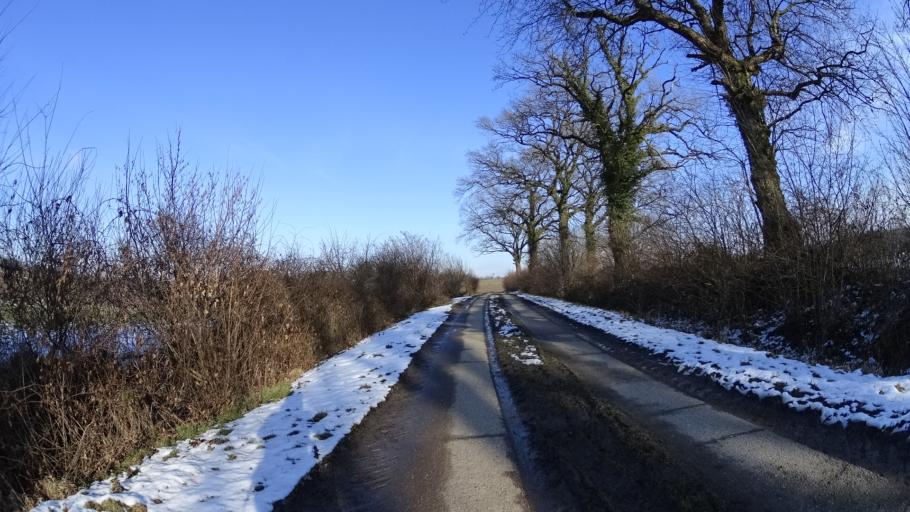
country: DE
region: Schleswig-Holstein
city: Martensrade
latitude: 54.2781
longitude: 10.3762
